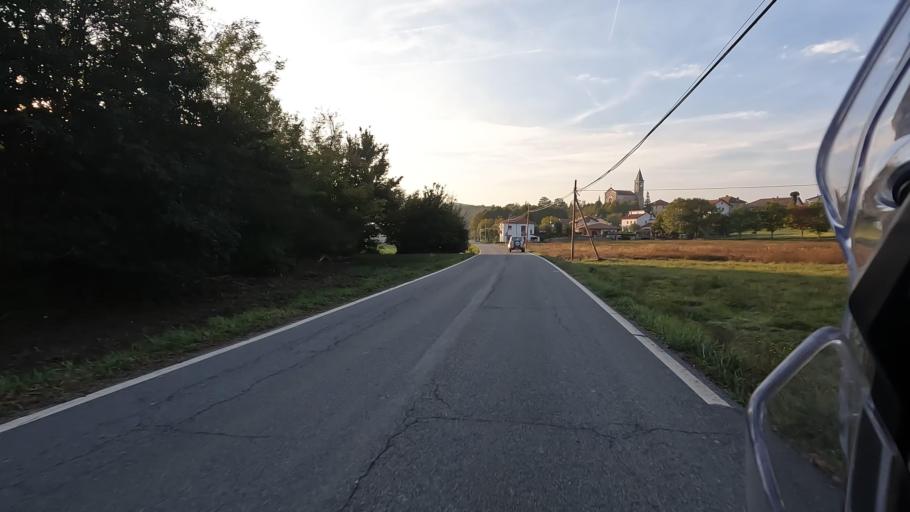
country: IT
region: Liguria
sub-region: Provincia di Savona
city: Sassello
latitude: 44.4996
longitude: 8.4913
